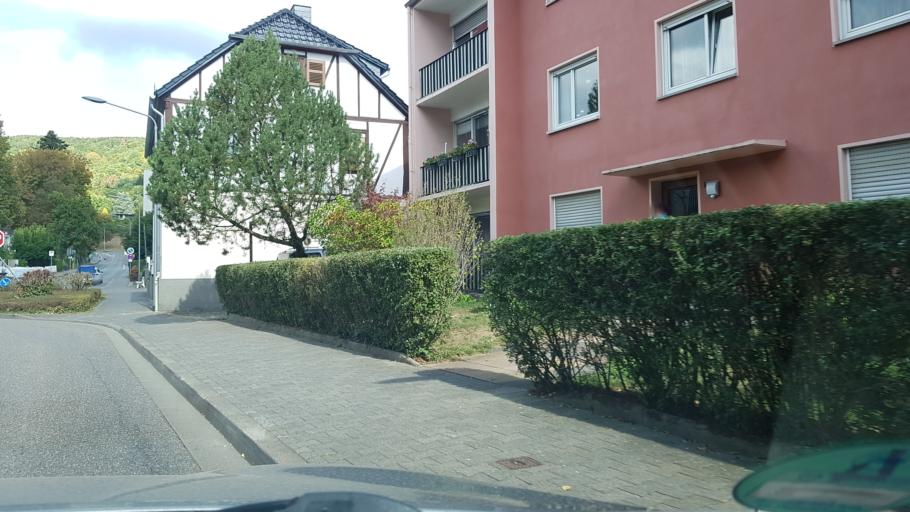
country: DE
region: Rheinland-Pfalz
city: Nassau
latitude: 50.3150
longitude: 7.7956
